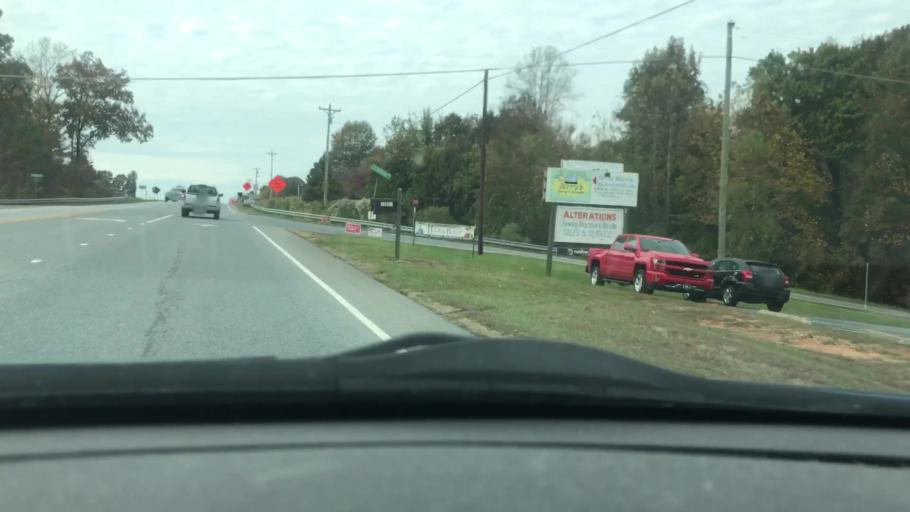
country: US
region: North Carolina
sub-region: Randolph County
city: Asheboro
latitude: 35.6913
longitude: -79.8500
